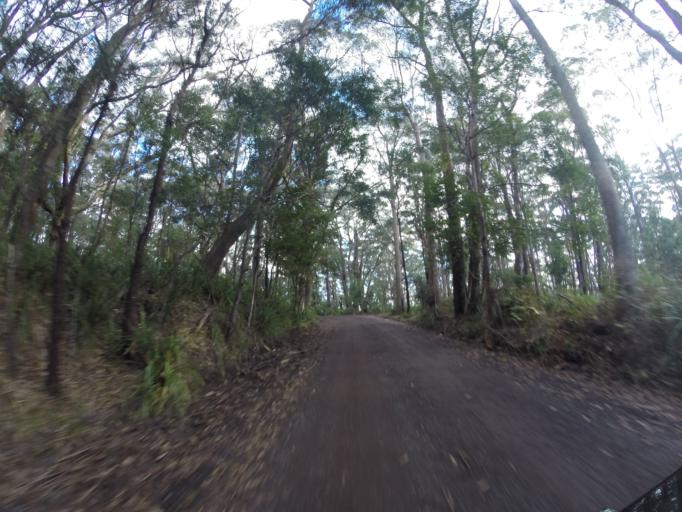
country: AU
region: New South Wales
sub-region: Wollongong
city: Cordeaux Heights
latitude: -34.4304
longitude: 150.7823
